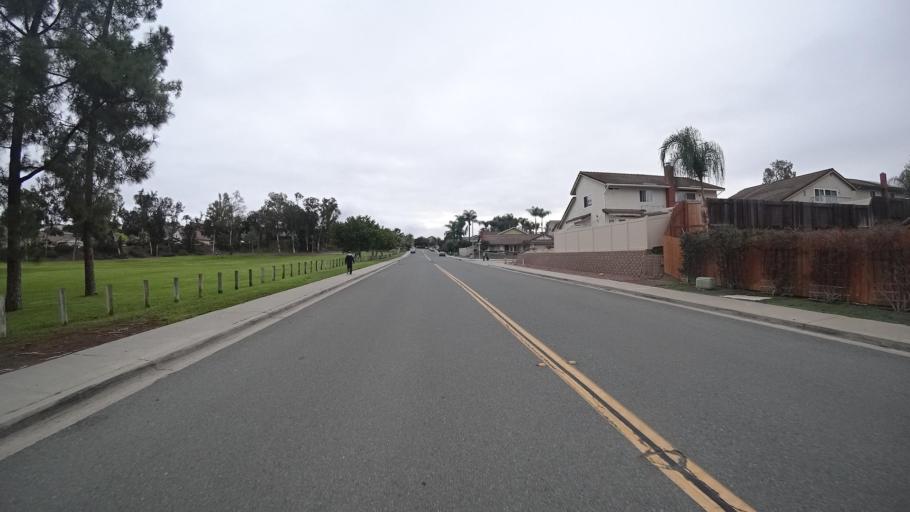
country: US
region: California
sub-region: San Diego County
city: Rancho San Diego
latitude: 32.7513
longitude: -116.9170
